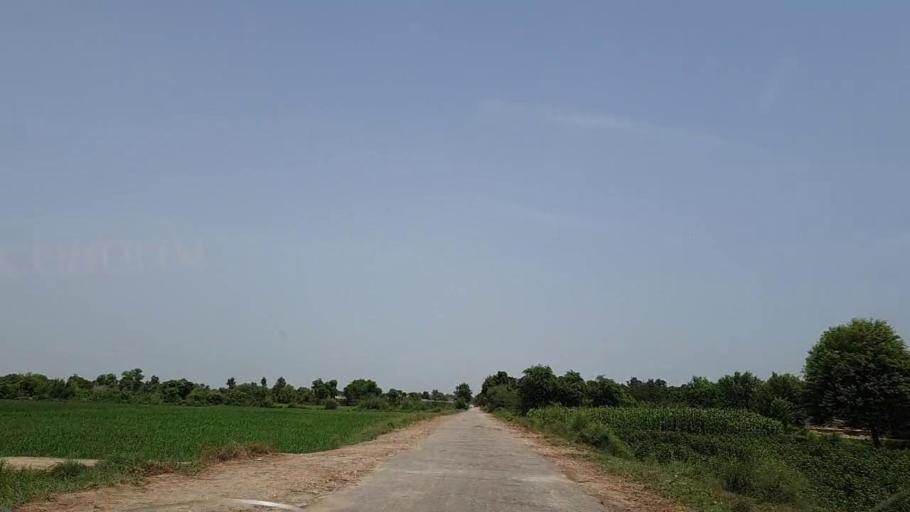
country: PK
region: Sindh
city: Tharu Shah
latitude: 26.9464
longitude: 68.0253
